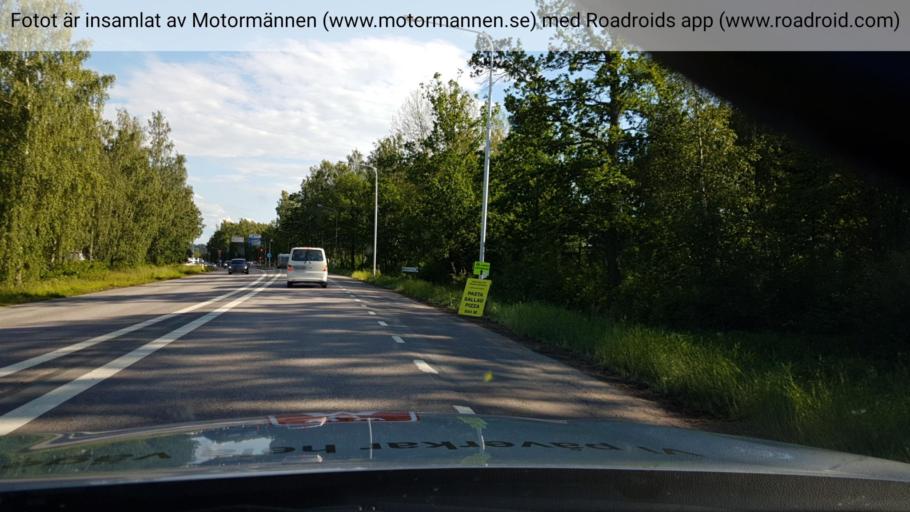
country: SE
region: OEstergoetland
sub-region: Motala Kommun
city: Motala
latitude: 58.5582
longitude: 15.0620
